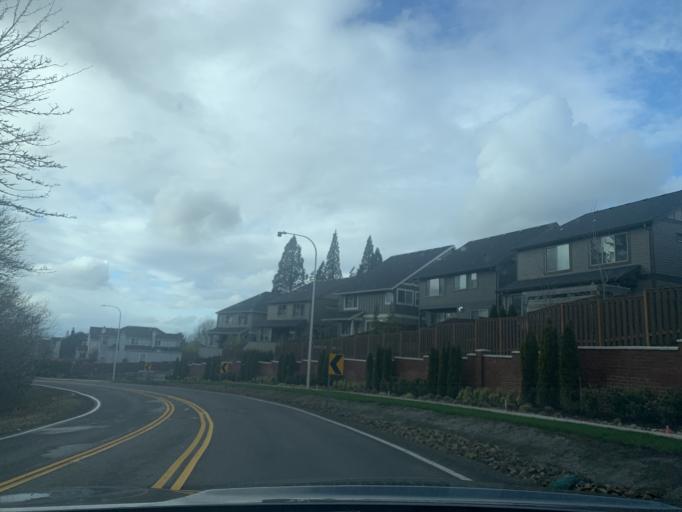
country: US
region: Oregon
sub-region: Washington County
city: Cedar Mill
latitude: 45.5488
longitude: -122.8037
